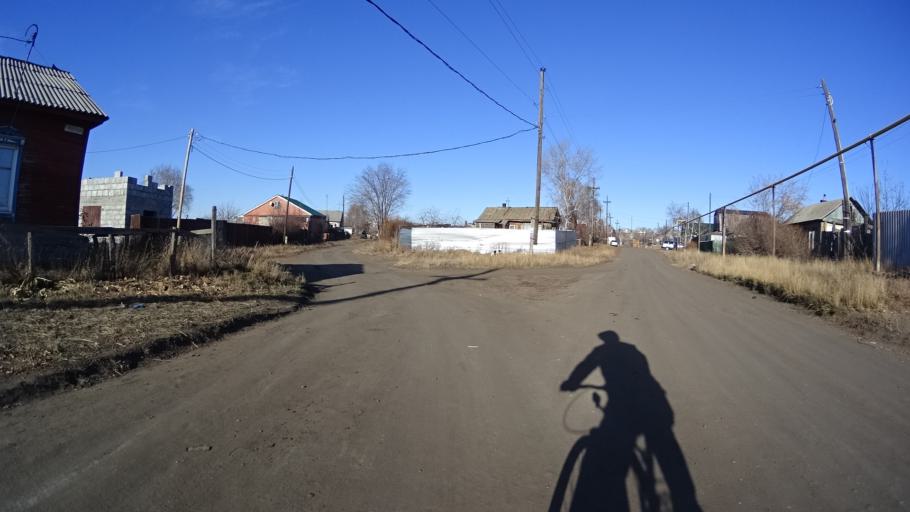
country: RU
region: Chelyabinsk
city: Troitsk
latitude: 54.0915
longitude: 61.5872
